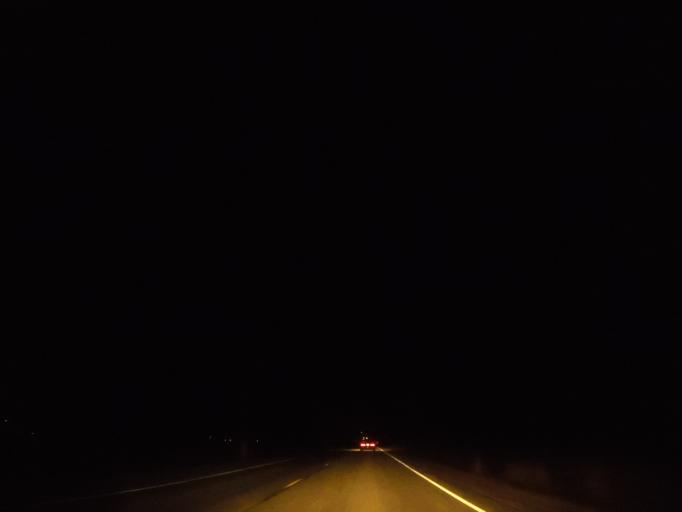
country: US
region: Indiana
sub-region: Newton County
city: Goodland
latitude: 40.7658
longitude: -87.3525
